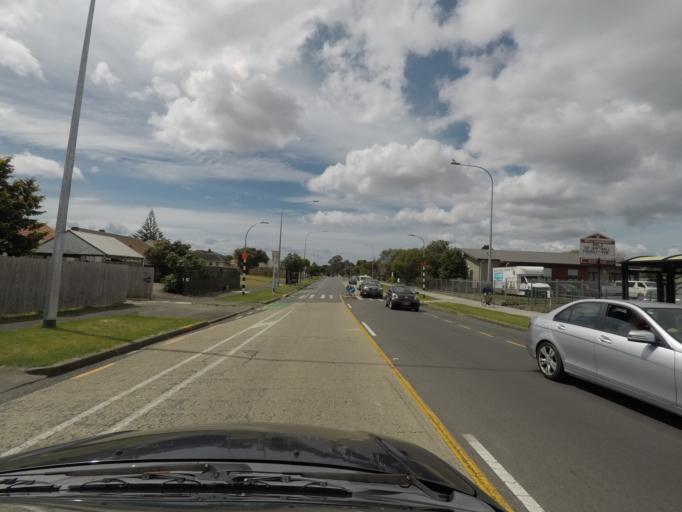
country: NZ
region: Auckland
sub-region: Auckland
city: Auckland
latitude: -36.9030
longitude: 174.7292
